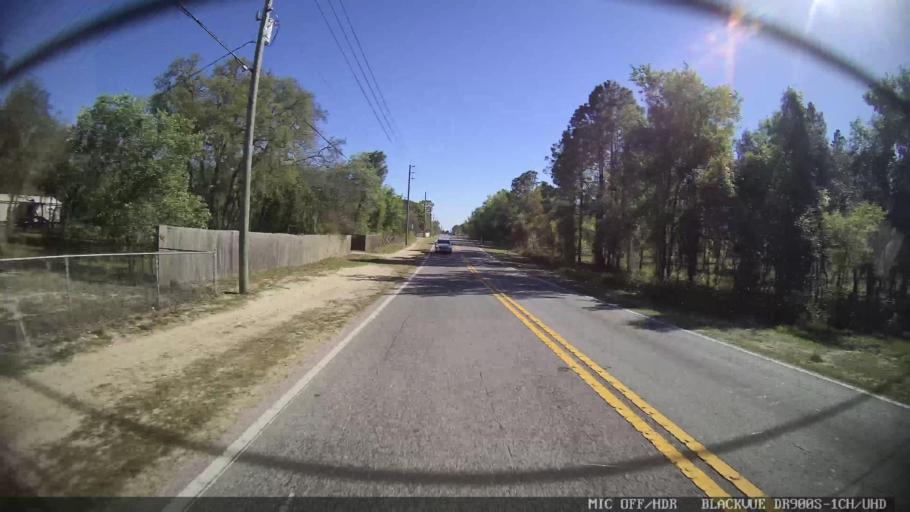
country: US
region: Florida
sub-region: Pasco County
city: Shady Hills
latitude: 28.3873
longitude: -82.5512
